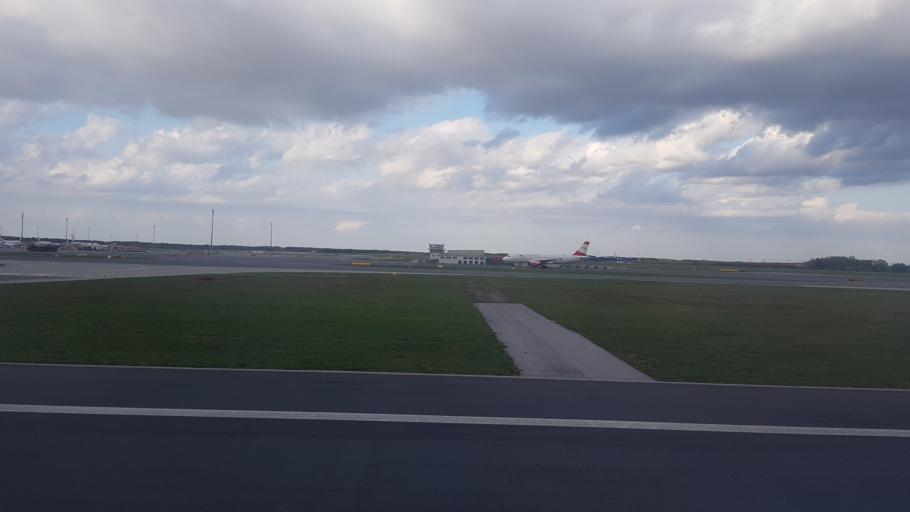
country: AT
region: Lower Austria
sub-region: Politischer Bezirk Bruck an der Leitha
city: Enzersdorf an der Fischa
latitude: 48.1100
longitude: 16.5725
